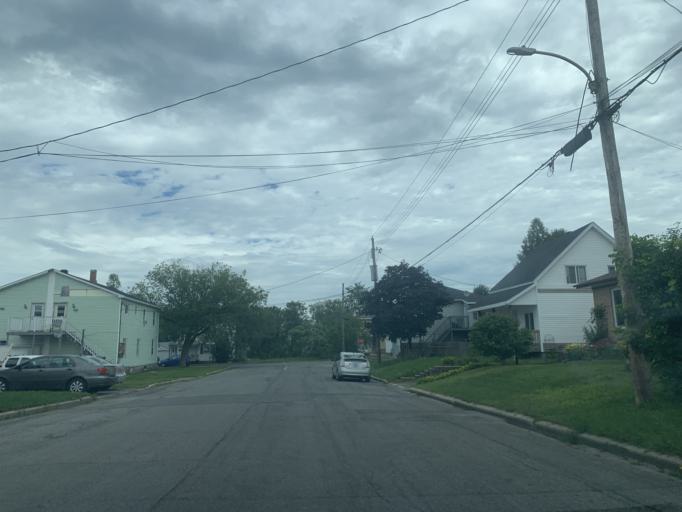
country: CA
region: Ontario
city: Hawkesbury
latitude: 45.6088
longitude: -74.5941
